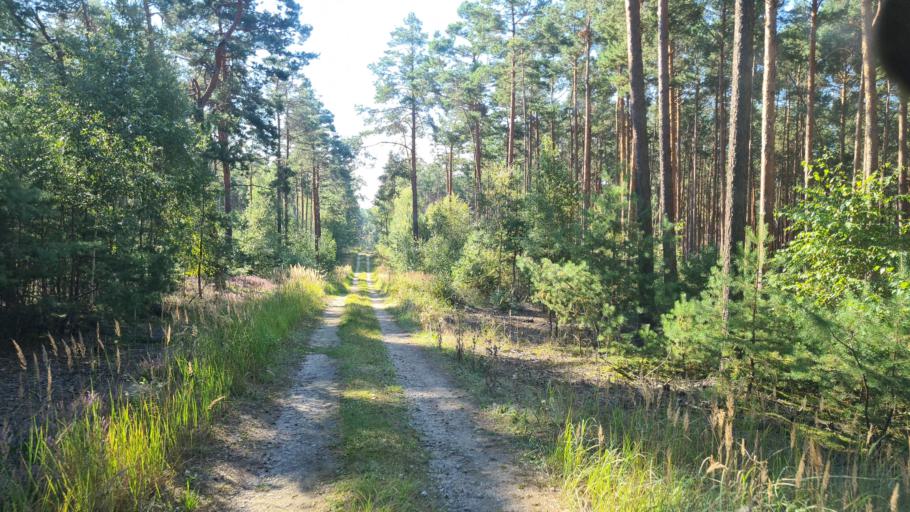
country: DE
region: Brandenburg
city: Schonborn
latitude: 51.6340
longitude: 13.5035
